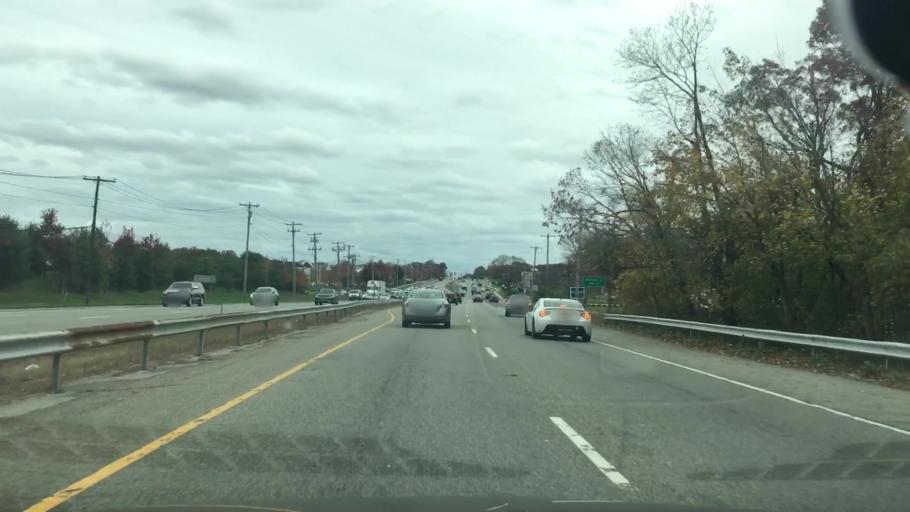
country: US
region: New York
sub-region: Suffolk County
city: Lake Grove
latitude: 40.8678
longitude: -73.1335
